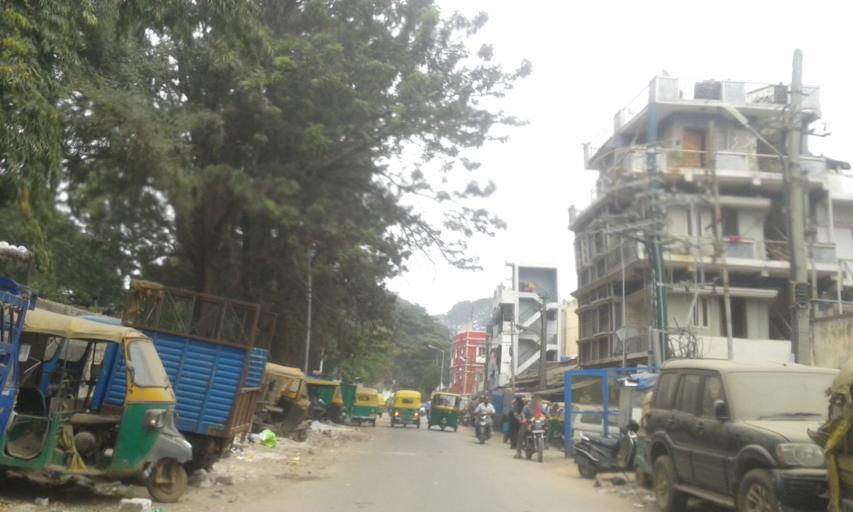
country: IN
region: Karnataka
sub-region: Bangalore Urban
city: Bangalore
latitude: 12.9553
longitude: 77.6113
